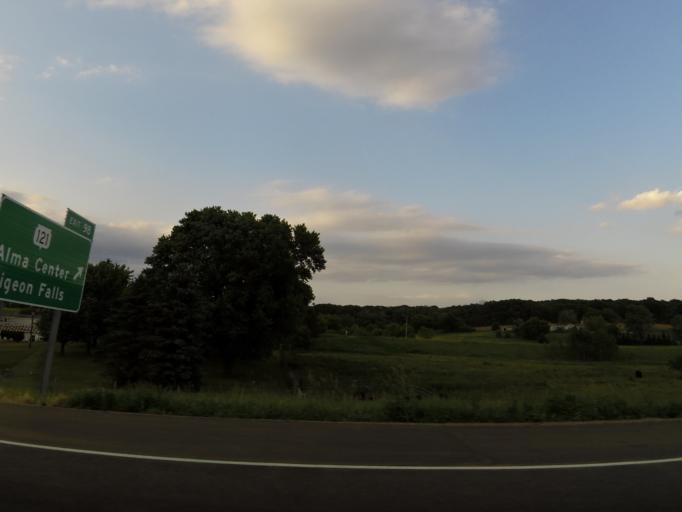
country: US
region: Wisconsin
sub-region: Trempealeau County
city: Osseo
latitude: 44.4546
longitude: -91.0874
